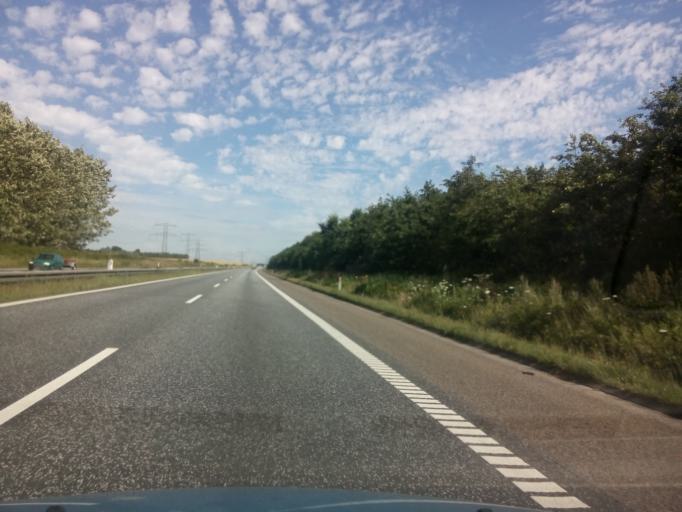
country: DK
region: Central Jutland
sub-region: Arhus Kommune
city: Trige
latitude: 56.2565
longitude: 10.1257
